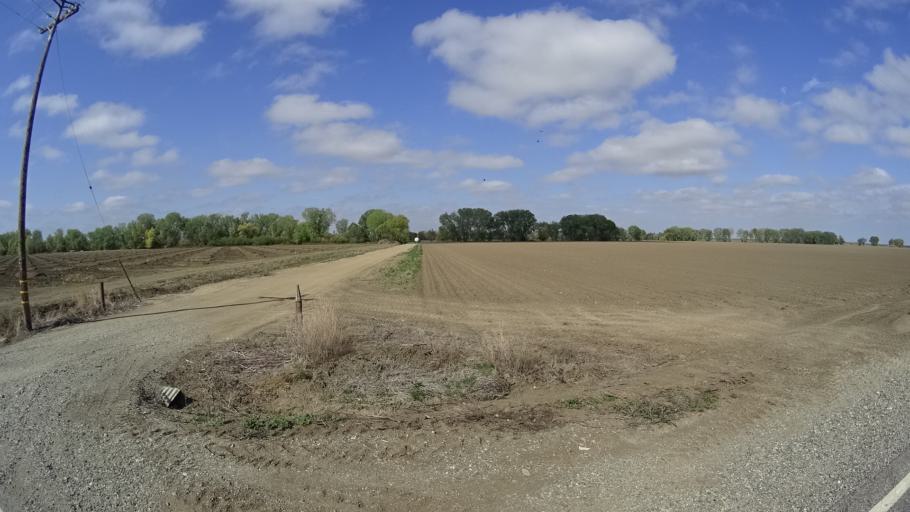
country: US
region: California
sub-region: Colusa County
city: Colusa
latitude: 39.3981
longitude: -121.9284
